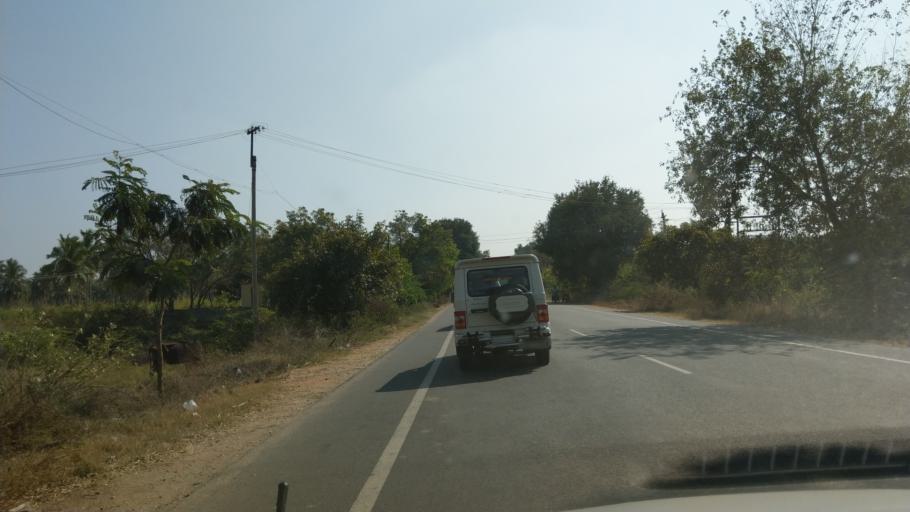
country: IN
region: Tamil Nadu
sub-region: Vellore
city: Arcot
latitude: 12.8832
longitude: 79.3175
